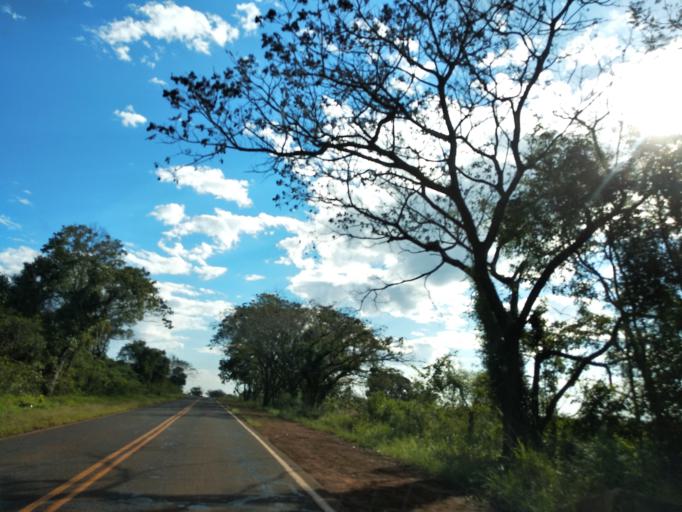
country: AR
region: Misiones
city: Jardin America
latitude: -27.0364
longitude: -55.2040
